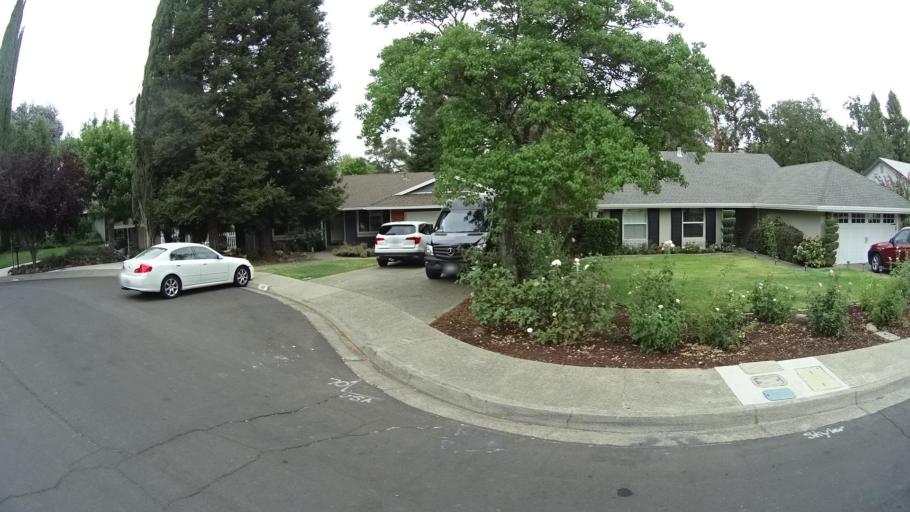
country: US
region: California
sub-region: Placer County
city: Rocklin
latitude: 38.7882
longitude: -121.2503
